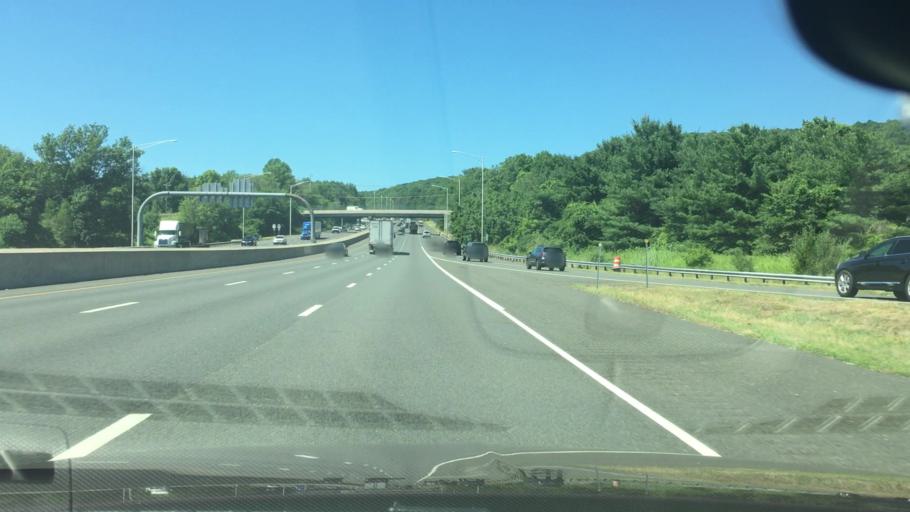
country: US
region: Connecticut
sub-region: New Haven County
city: Cheshire Village
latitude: 41.5585
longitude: -72.9232
